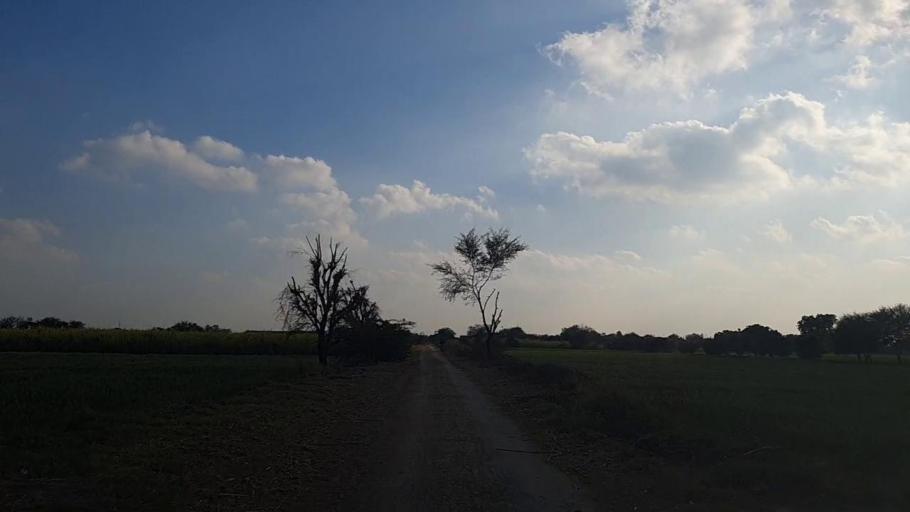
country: PK
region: Sindh
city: Tando Mittha Khan
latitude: 25.9407
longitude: 69.2148
